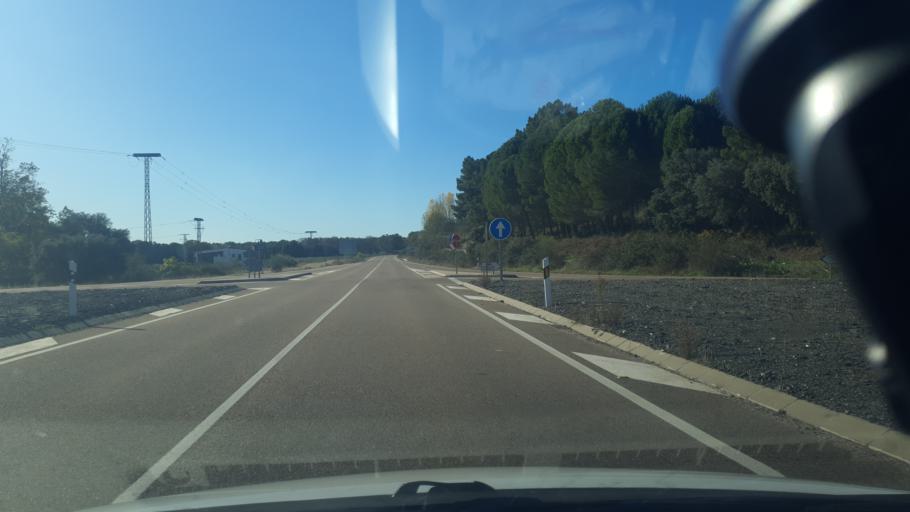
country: ES
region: Castille and Leon
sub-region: Provincia de Avila
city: Arenas de San Pedro
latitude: 40.1798
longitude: -5.0874
